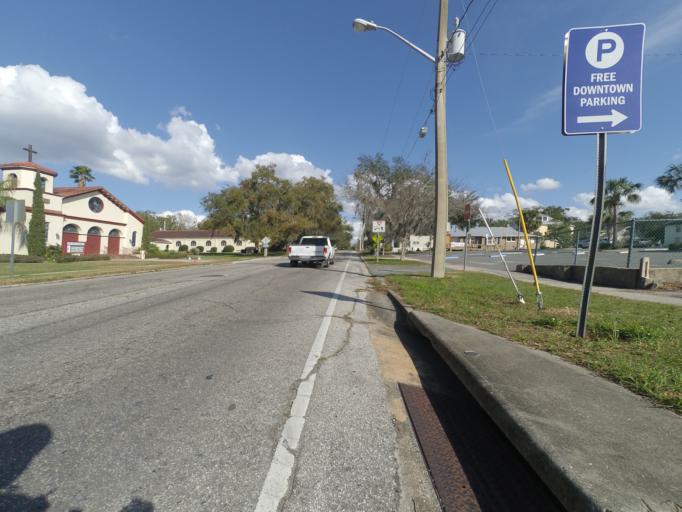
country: US
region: Florida
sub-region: Lake County
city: Mount Dora
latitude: 28.8005
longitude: -81.6417
